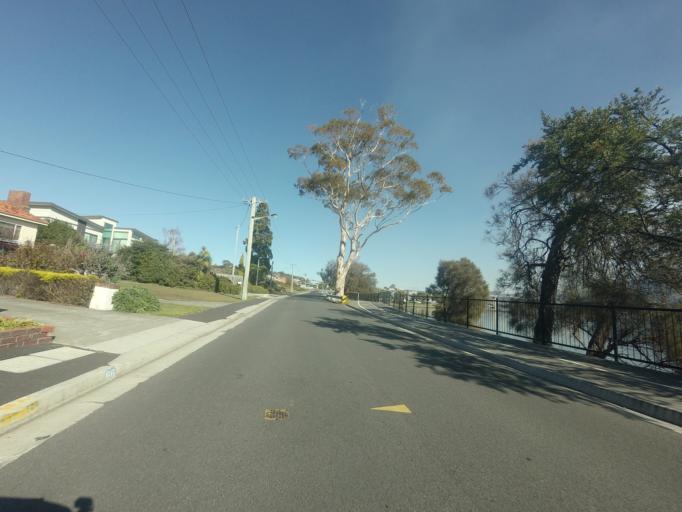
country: AU
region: Tasmania
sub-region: Clarence
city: Lindisfarne
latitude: -42.8553
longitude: 147.3554
